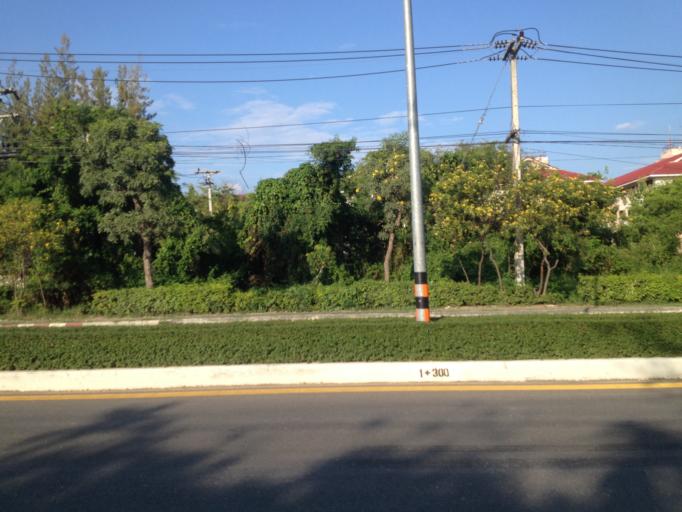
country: TH
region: Chiang Mai
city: Hang Dong
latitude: 18.7338
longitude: 98.9385
